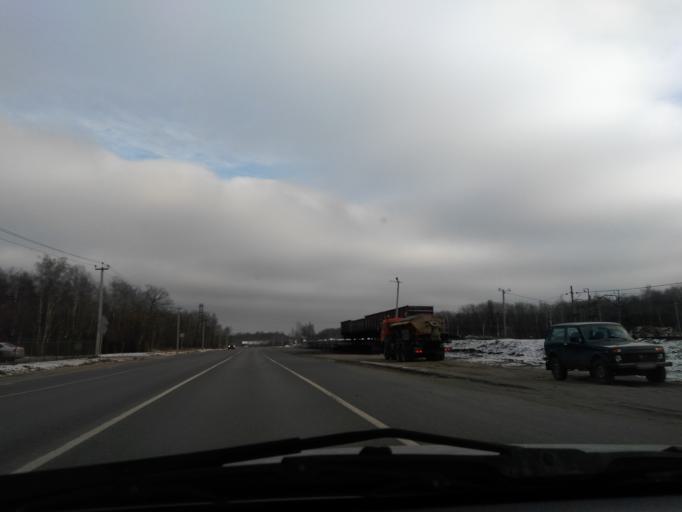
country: RU
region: Moskovskaya
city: Selyatino
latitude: 55.2748
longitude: 37.1197
